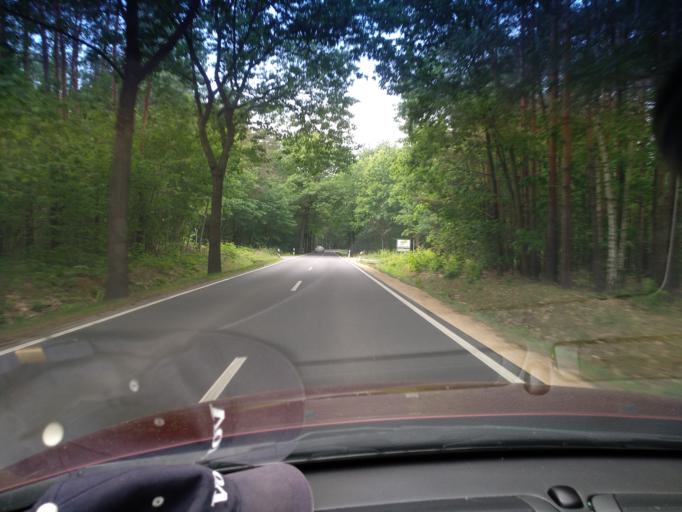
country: DE
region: Saxony
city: Quitzdorf
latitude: 51.3034
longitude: 14.7414
